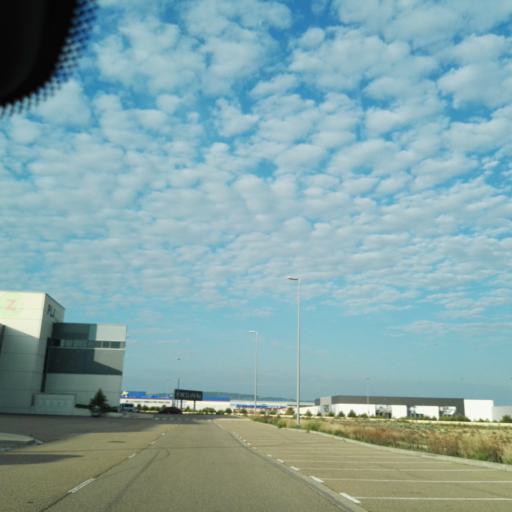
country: ES
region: Aragon
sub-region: Provincia de Zaragoza
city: Montecanal
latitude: 41.6495
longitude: -0.9957
